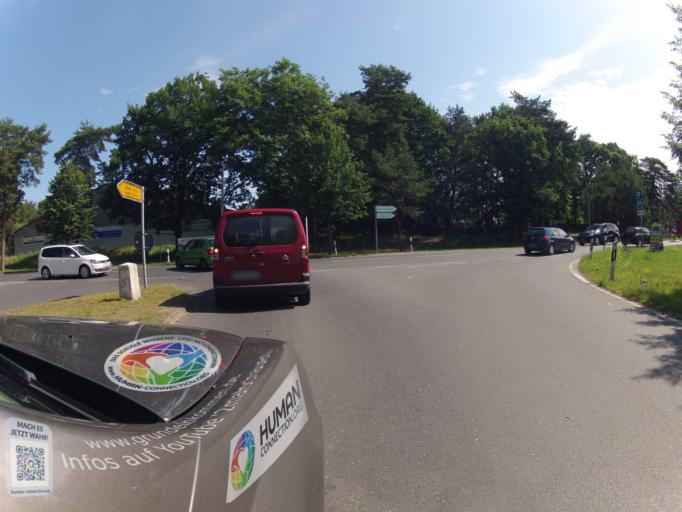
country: DE
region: Mecklenburg-Vorpommern
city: Seebad Heringsdorf
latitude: 53.9341
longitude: 14.1930
